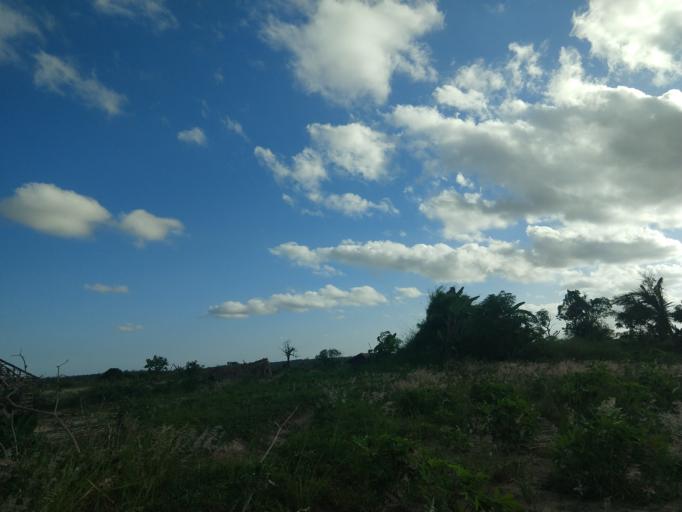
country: MZ
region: Sofala
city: Beira
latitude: -19.6072
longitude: 35.1439
